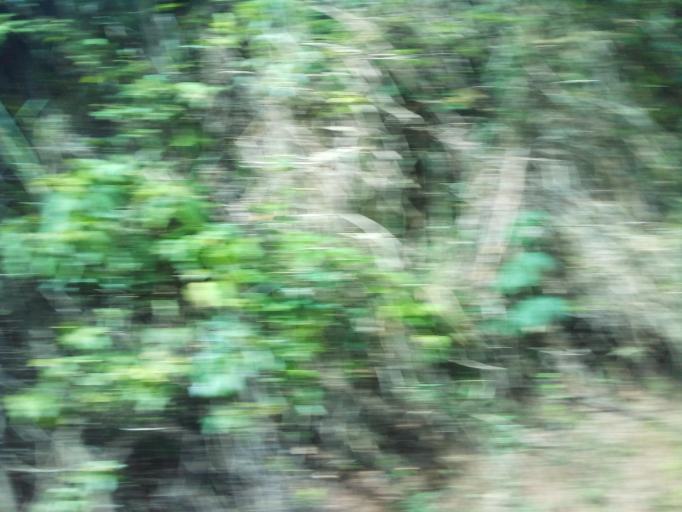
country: BR
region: Minas Gerais
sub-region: Santa Luzia
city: Santa Luzia
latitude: -19.8688
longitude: -43.8354
